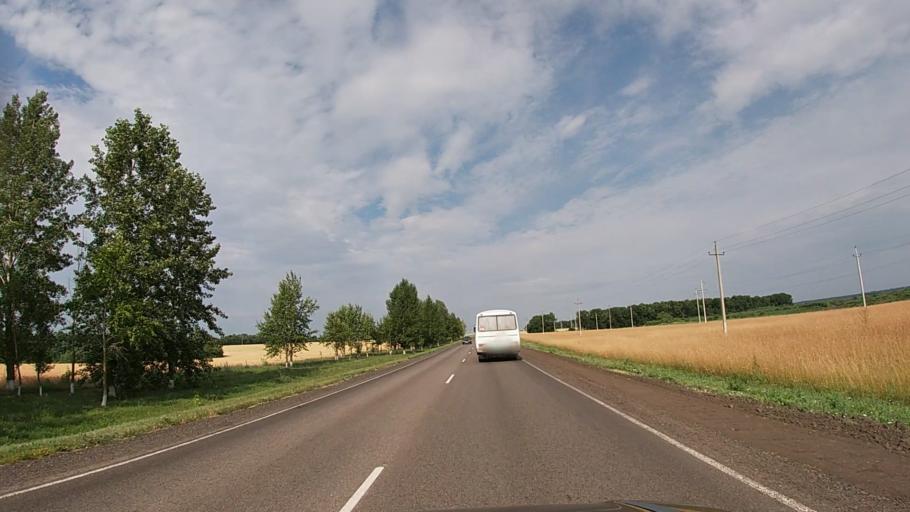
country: RU
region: Belgorod
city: Krasnaya Yaruga
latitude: 50.7980
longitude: 35.6054
